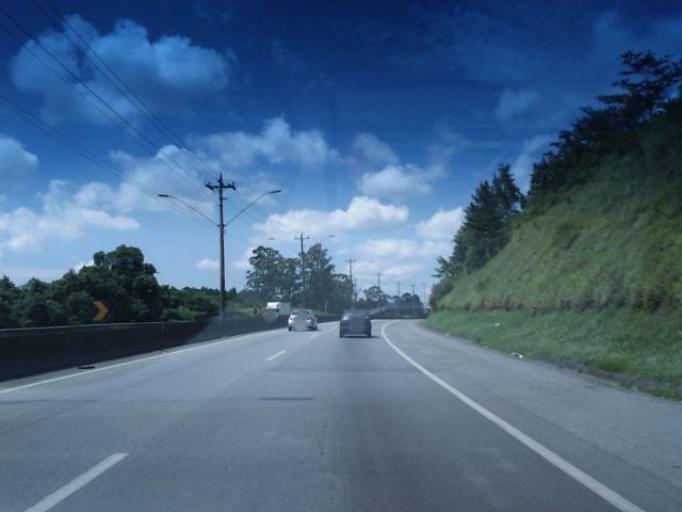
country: BR
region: Sao Paulo
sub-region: Itapecerica Da Serra
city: Itapecerica da Serra
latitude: -23.7580
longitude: -46.9028
